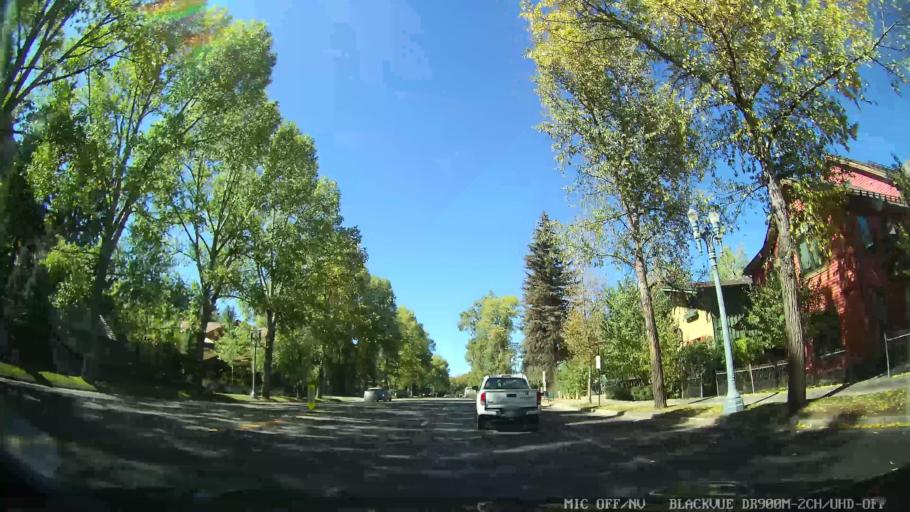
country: US
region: Colorado
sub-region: Pitkin County
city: Aspen
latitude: 39.1924
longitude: -106.8275
